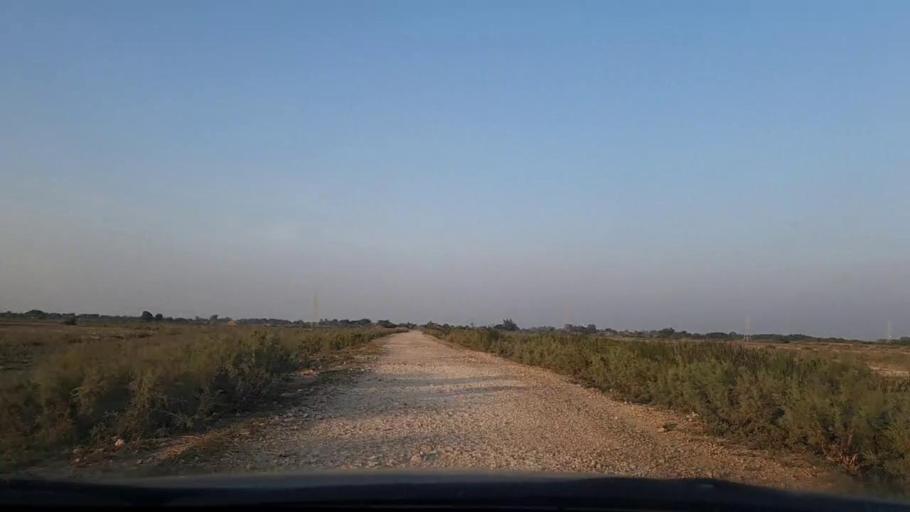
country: PK
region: Sindh
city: Mirpur Sakro
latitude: 24.5569
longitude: 67.6574
